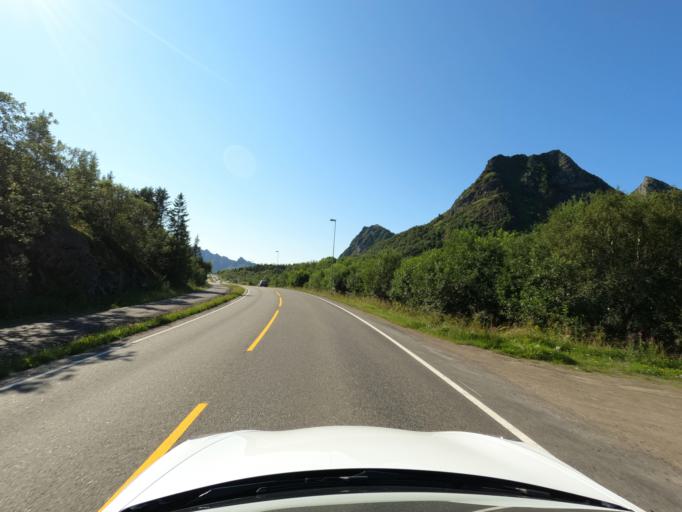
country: NO
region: Nordland
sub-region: Vagan
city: Kabelvag
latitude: 68.2156
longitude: 14.4348
